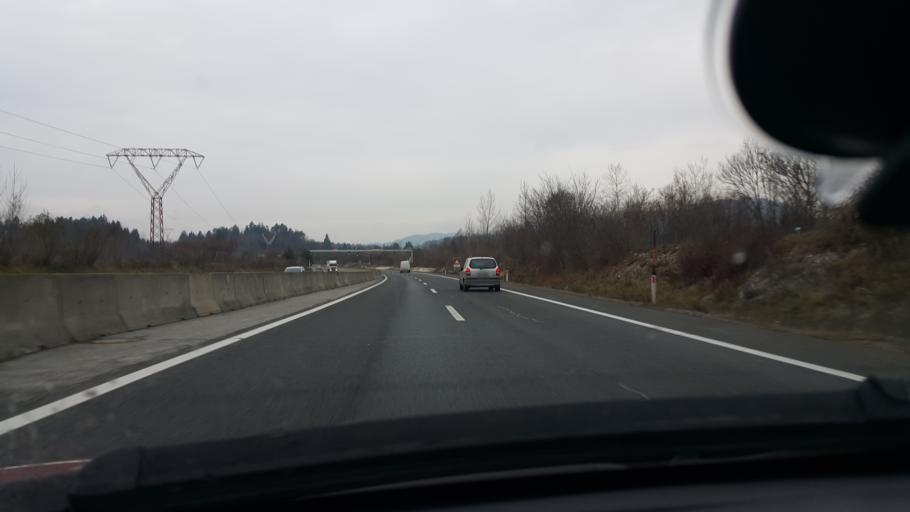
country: AT
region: Carinthia
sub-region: Politischer Bezirk Klagenfurt Land
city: Poggersdorf
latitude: 46.6454
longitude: 14.4162
